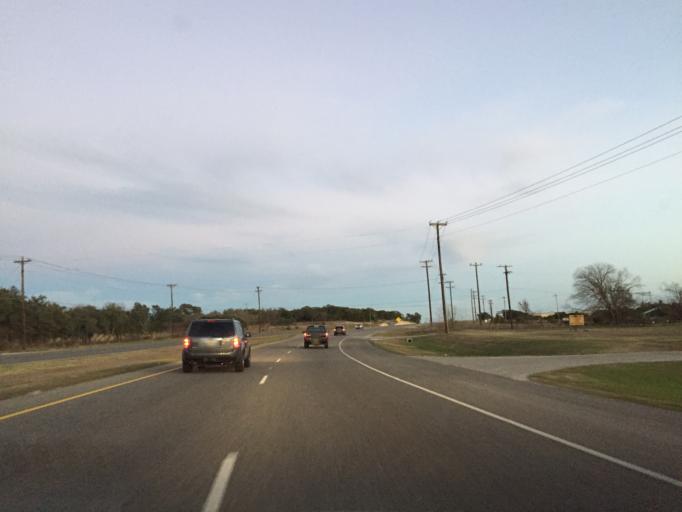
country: US
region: Texas
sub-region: Williamson County
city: Cedar Park
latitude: 30.5153
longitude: -97.8678
